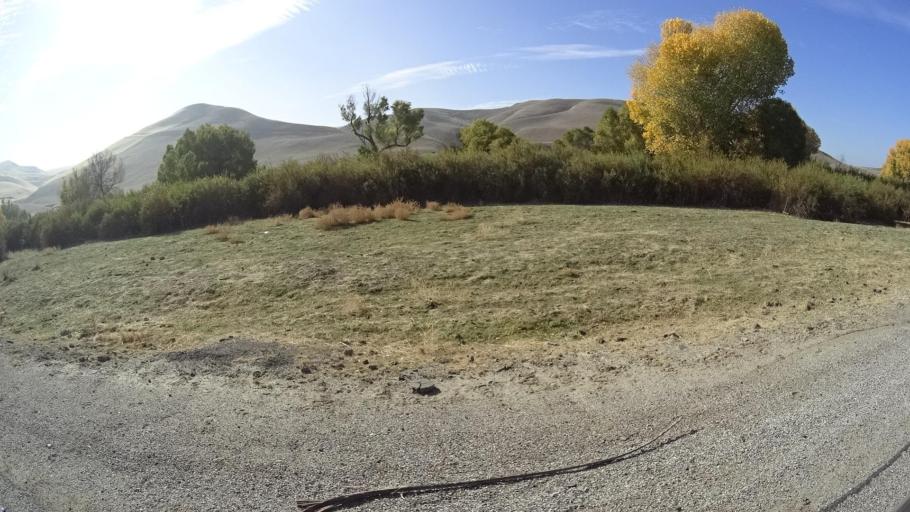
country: US
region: California
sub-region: Kern County
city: Oildale
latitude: 35.5185
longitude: -118.9280
